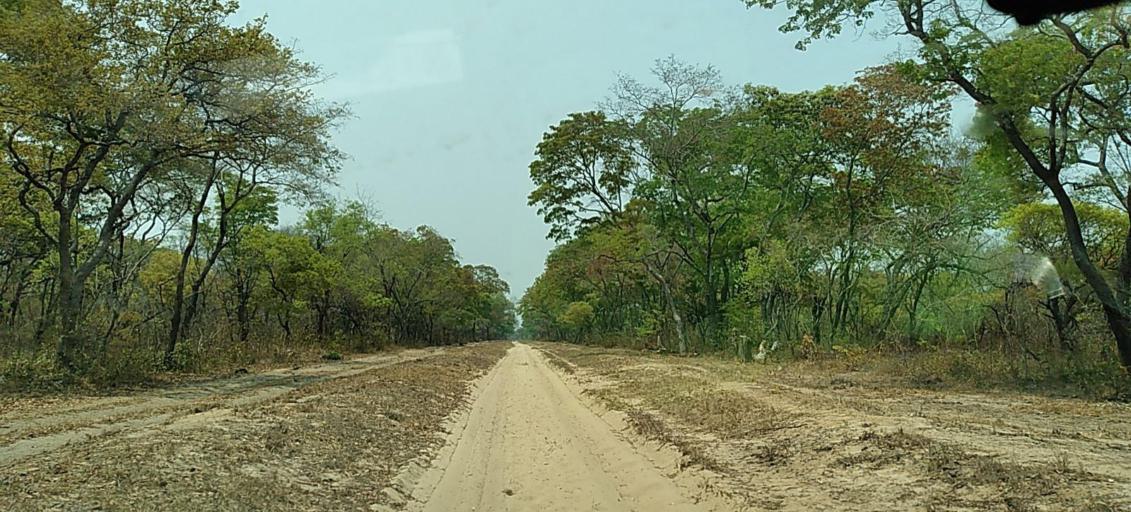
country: ZM
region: Western
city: Lukulu
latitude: -14.1354
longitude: 23.2752
